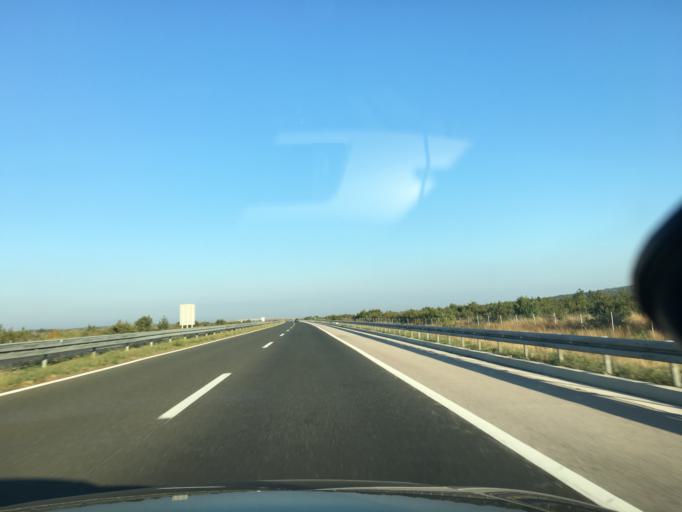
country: HR
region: Zadarska
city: Benkovac
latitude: 43.9480
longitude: 15.6907
